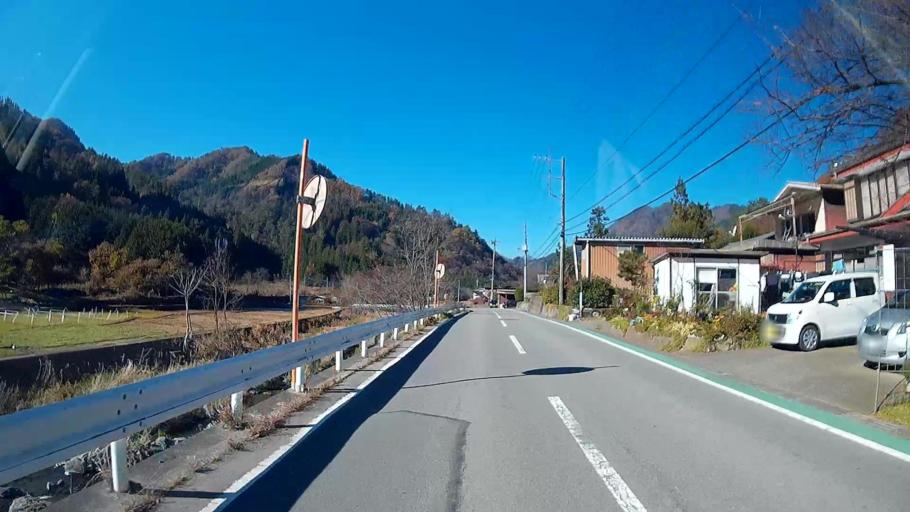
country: JP
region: Yamanashi
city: Otsuki
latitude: 35.5601
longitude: 138.9822
